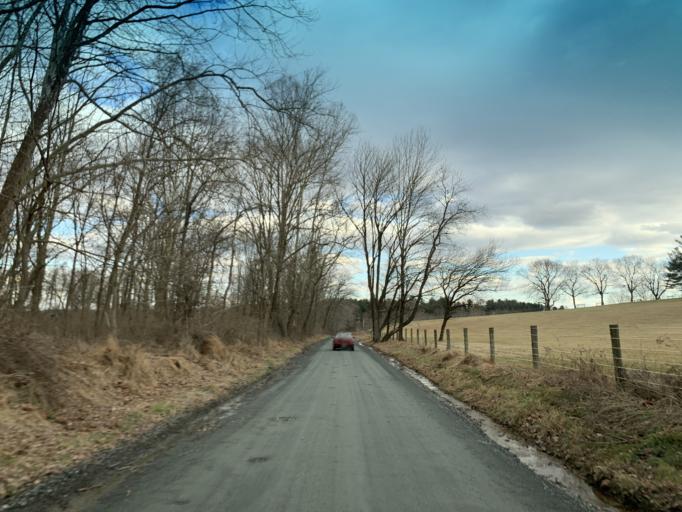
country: US
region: Maryland
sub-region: Harford County
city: South Bel Air
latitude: 39.5941
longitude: -76.2920
